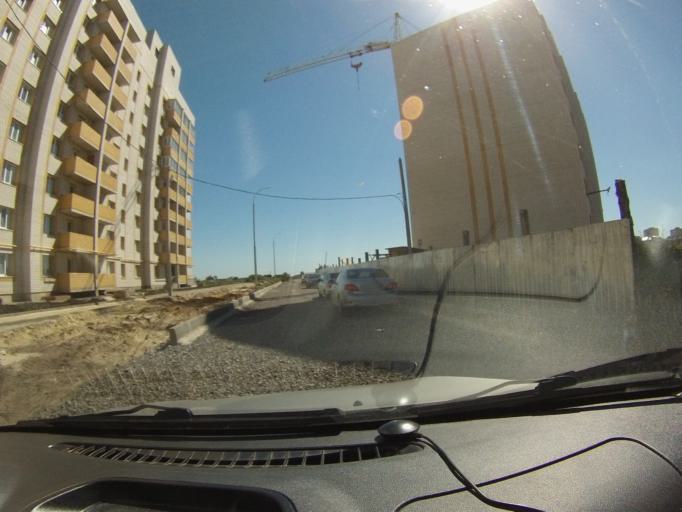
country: RU
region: Tambov
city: Tambov
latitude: 52.7760
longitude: 41.4123
